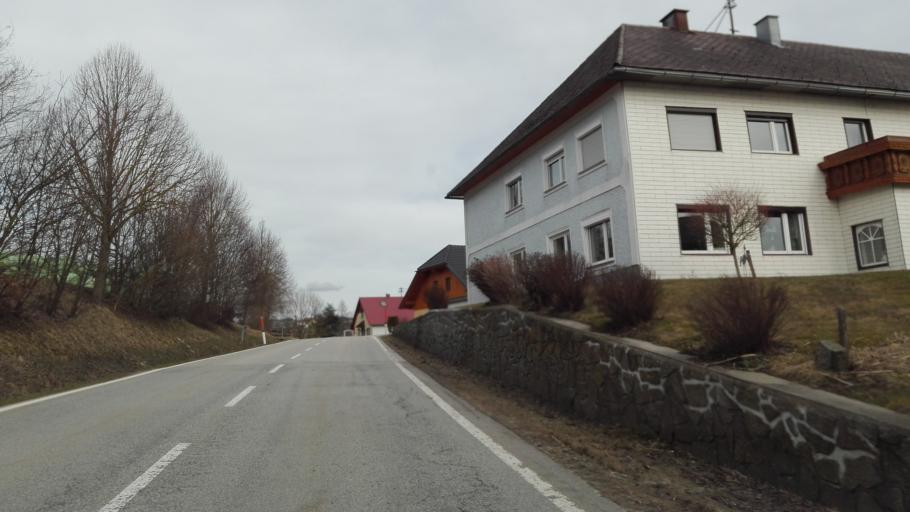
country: DE
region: Bavaria
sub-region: Lower Bavaria
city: Wegscheid
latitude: 48.6049
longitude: 13.8197
